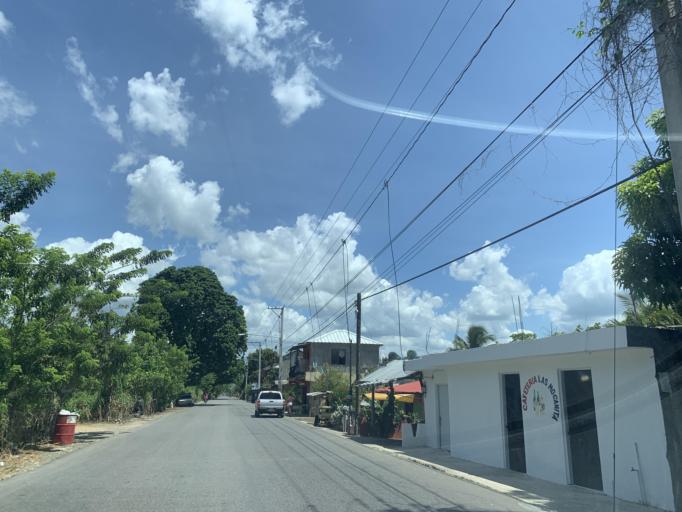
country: DO
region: Puerto Plata
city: Cabarete
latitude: 19.6999
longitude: -70.3826
